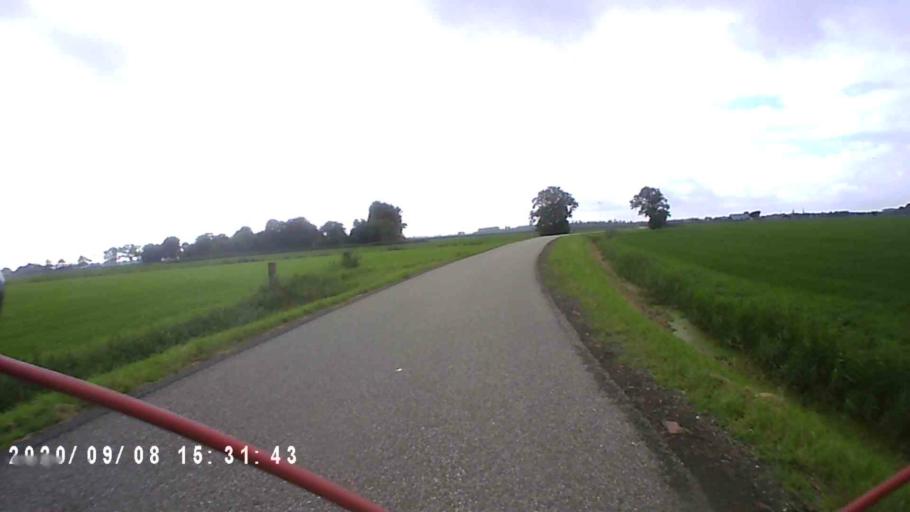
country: NL
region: Groningen
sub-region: Gemeente Bedum
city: Bedum
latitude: 53.2952
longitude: 6.6366
